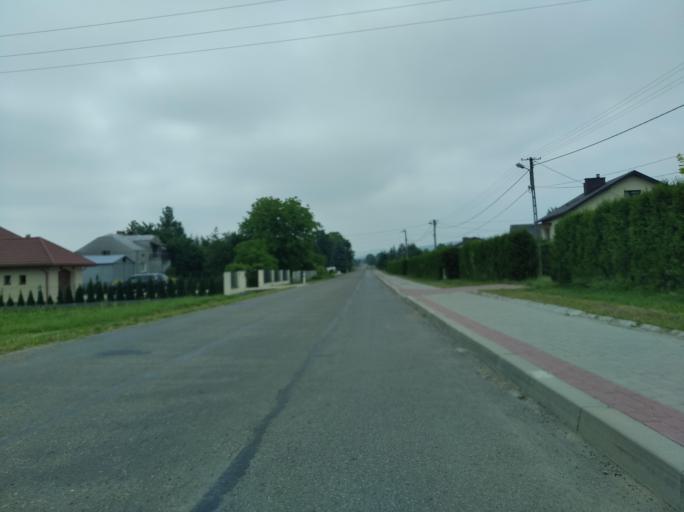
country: PL
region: Subcarpathian Voivodeship
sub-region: Powiat krosnienski
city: Sieniawa
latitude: 49.5756
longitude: 21.9235
